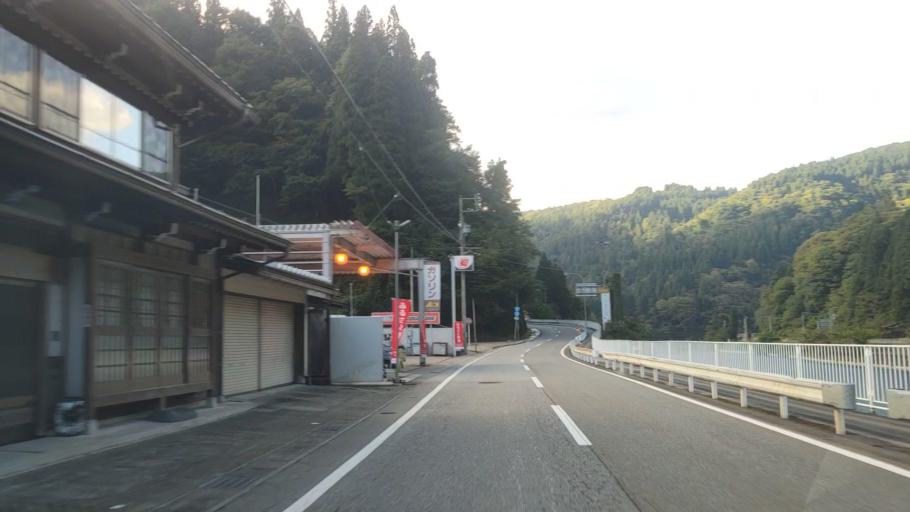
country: JP
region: Gifu
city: Takayama
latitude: 36.3021
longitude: 137.1124
